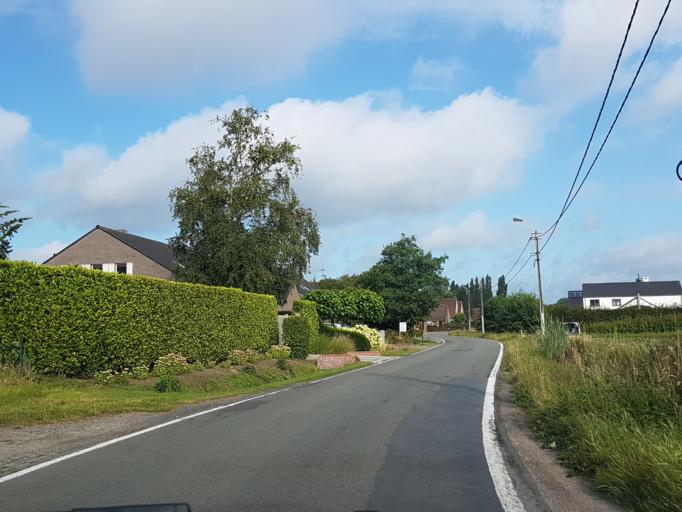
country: BE
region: Flanders
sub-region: Provincie Oost-Vlaanderen
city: Sint-Martens-Latem
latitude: 51.0595
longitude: 3.6384
